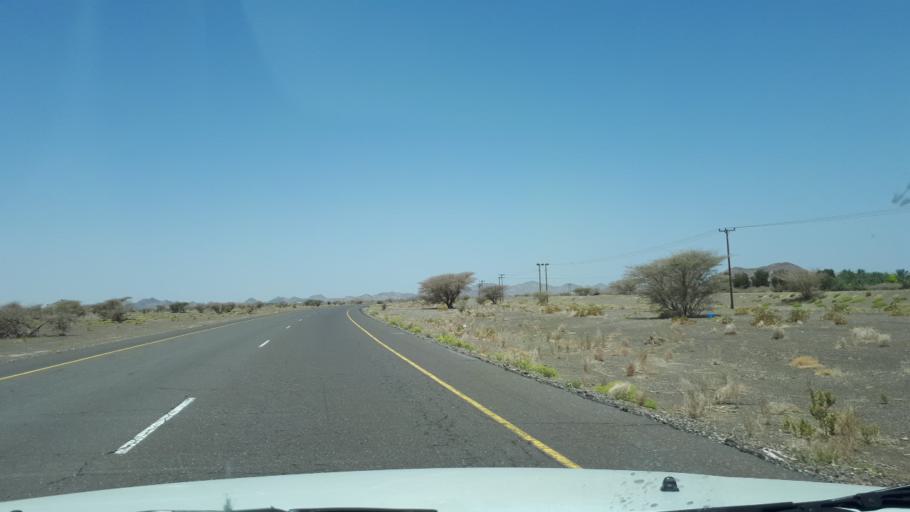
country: OM
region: Ash Sharqiyah
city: Ibra'
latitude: 22.6171
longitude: 58.4225
